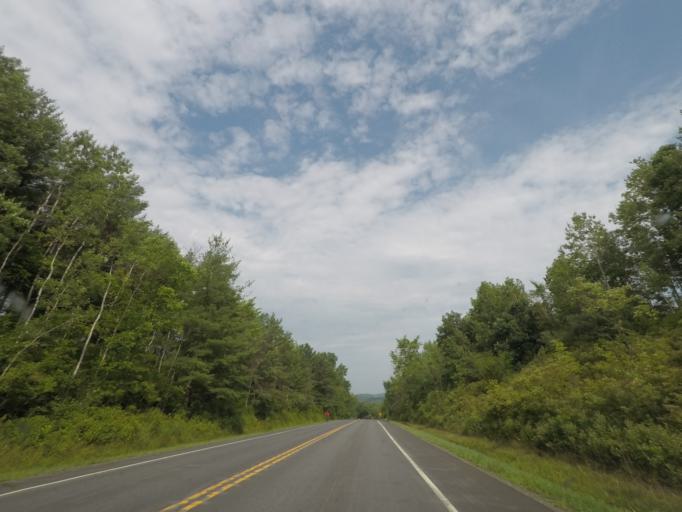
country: US
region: New York
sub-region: Rensselaer County
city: Poestenkill
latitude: 42.7302
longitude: -73.5588
